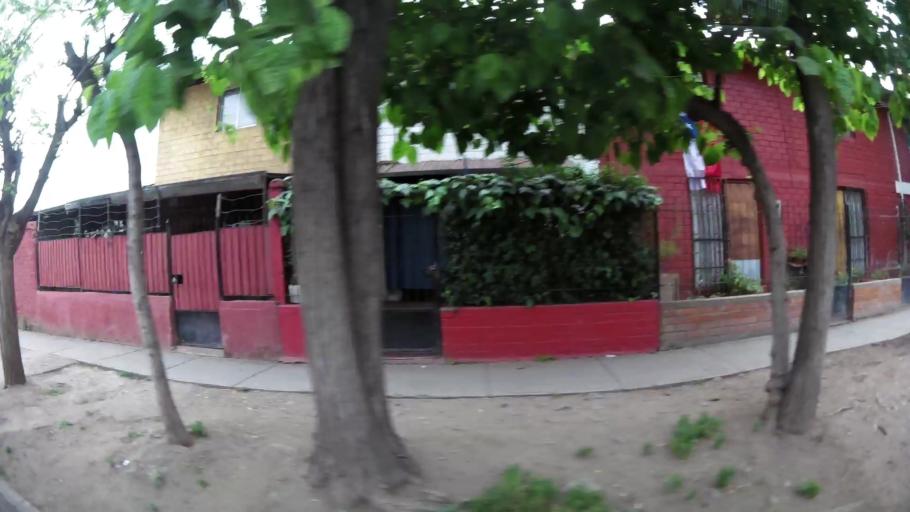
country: CL
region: Santiago Metropolitan
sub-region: Provincia de Chacabuco
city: Chicureo Abajo
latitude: -33.1983
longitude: -70.6752
